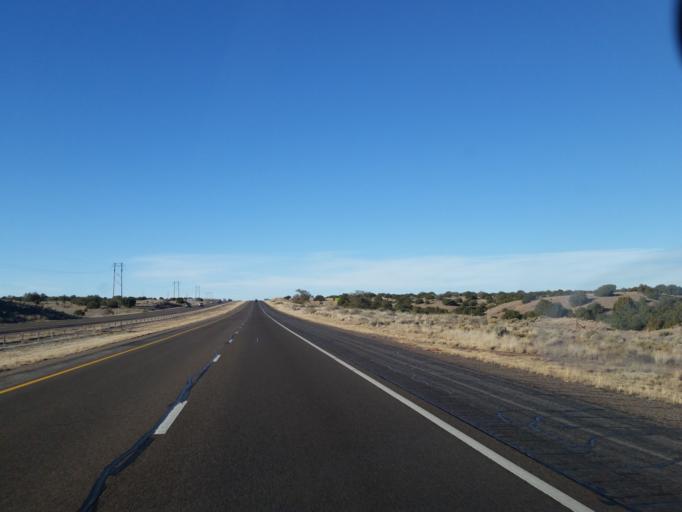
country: US
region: New Mexico
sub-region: Sandoval County
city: Santo Domingo Pueblo
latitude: 35.4773
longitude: -106.2878
